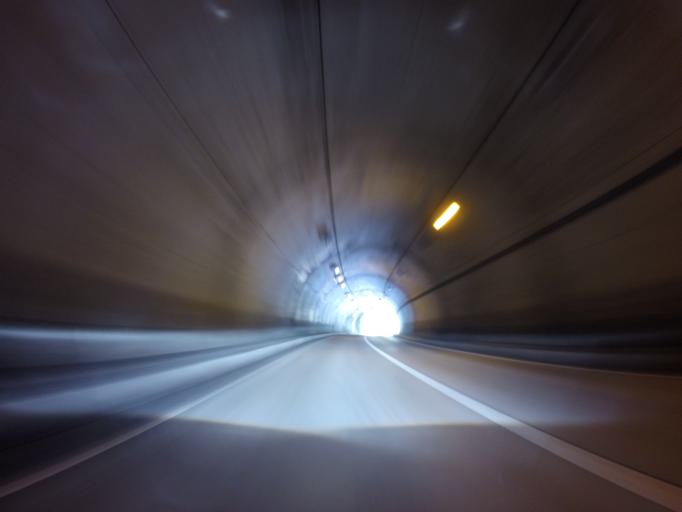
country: JP
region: Shizuoka
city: Shizuoka-shi
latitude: 35.2263
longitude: 138.3467
